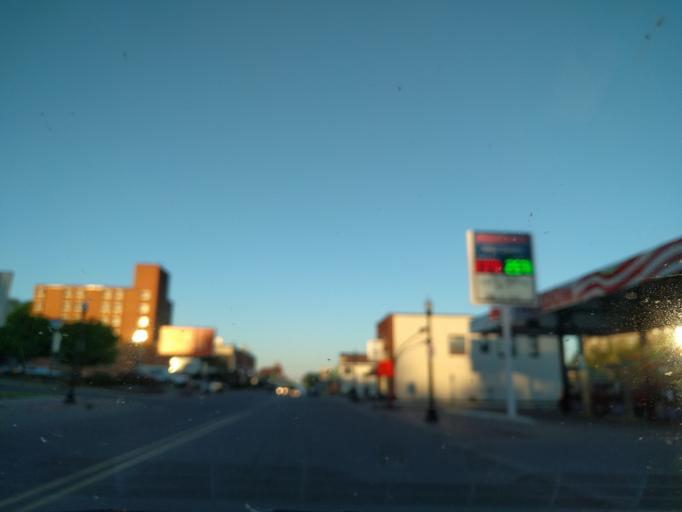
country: US
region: Michigan
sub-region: Marquette County
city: Marquette
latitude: 46.5446
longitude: -87.4025
